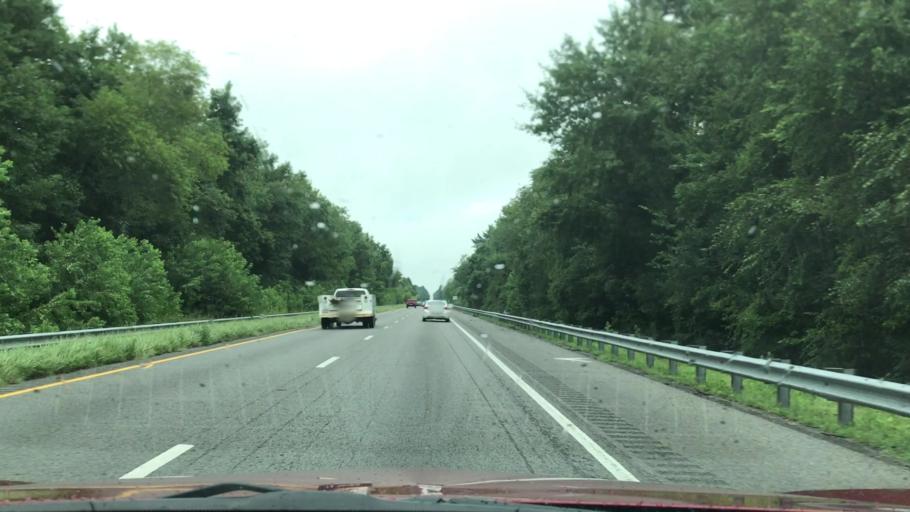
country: US
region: South Carolina
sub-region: Dorchester County
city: Ridgeville
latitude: 33.1487
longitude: -80.3347
